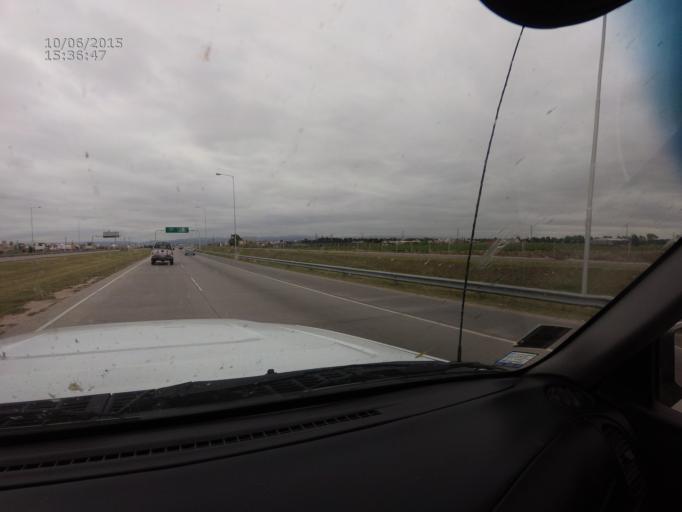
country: AR
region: Cordoba
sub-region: Departamento de Capital
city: Cordoba
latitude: -31.3549
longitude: -64.2131
